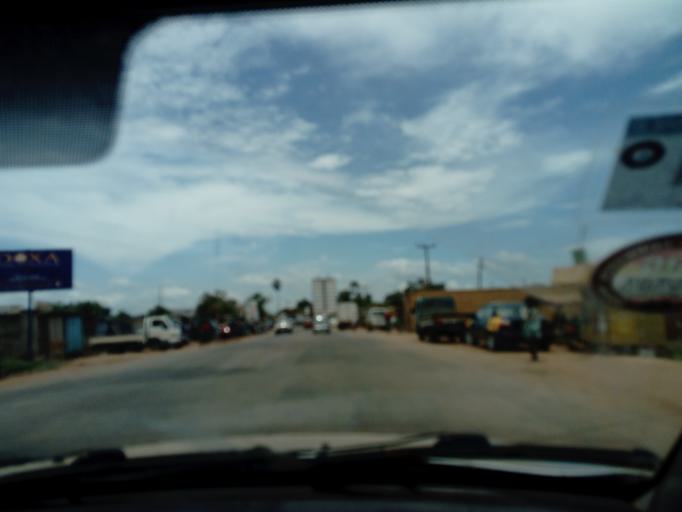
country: GH
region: Central
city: Cape Coast
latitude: 5.1356
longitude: -1.2776
